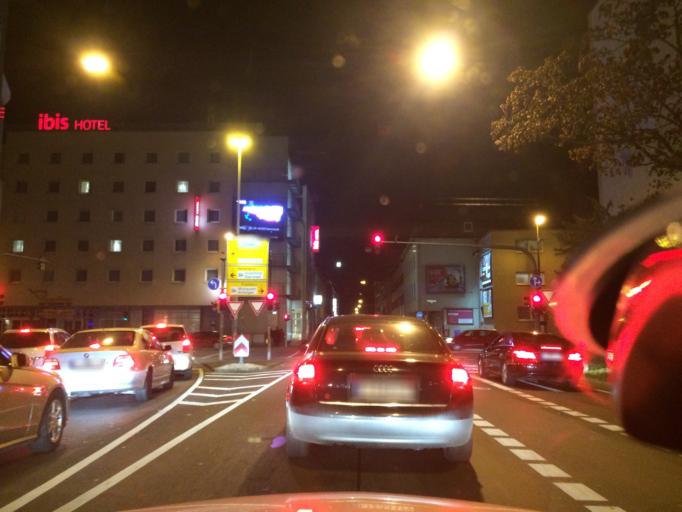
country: DE
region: Hesse
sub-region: Regierungsbezirk Darmstadt
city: Darmstadt
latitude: 49.8732
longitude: 8.6446
